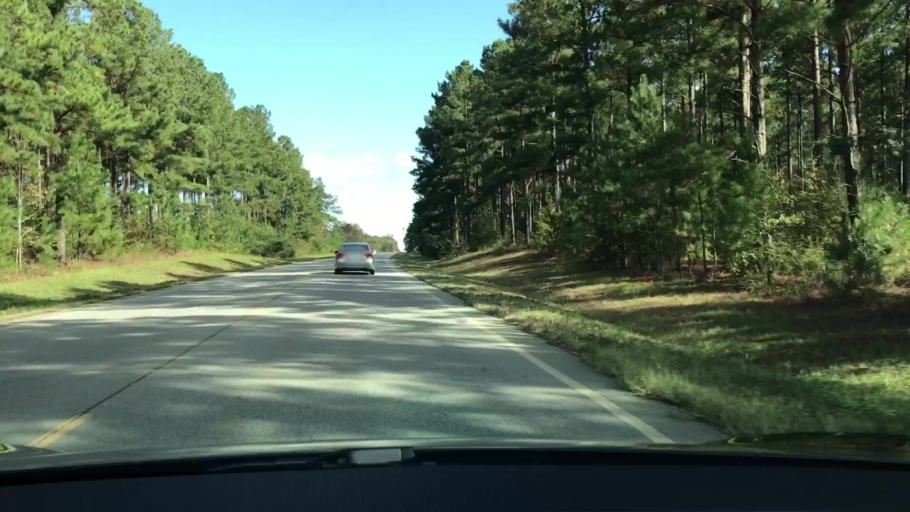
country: US
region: Georgia
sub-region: Jefferson County
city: Wrens
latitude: 33.2394
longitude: -82.4556
